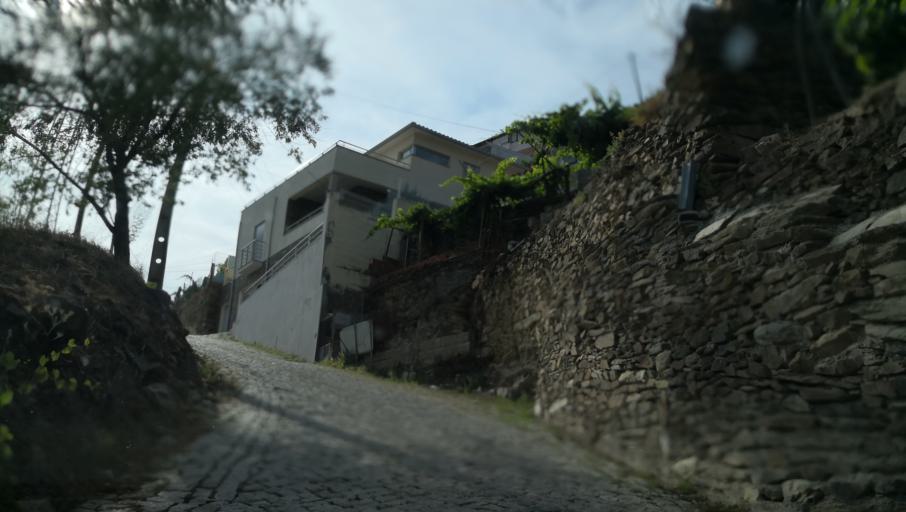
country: PT
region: Vila Real
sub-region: Sabrosa
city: Vilela
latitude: 41.1978
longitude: -7.5460
